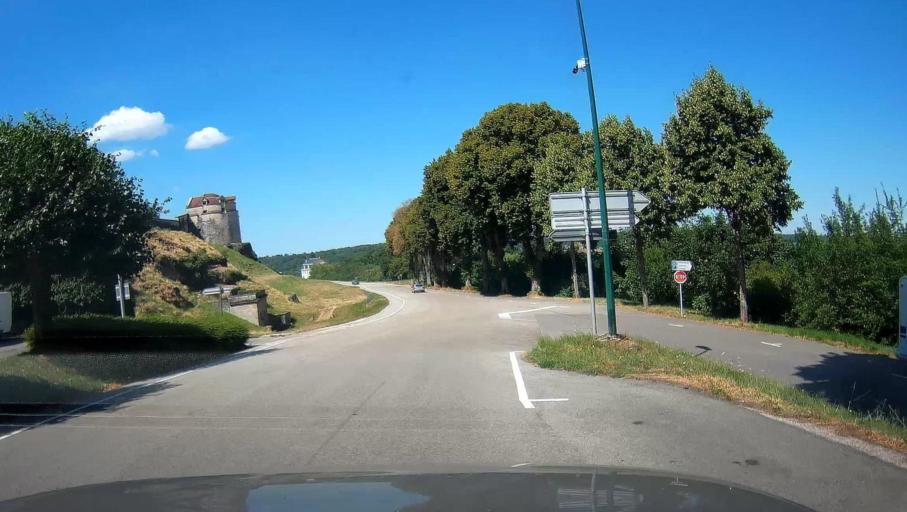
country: FR
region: Champagne-Ardenne
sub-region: Departement de la Haute-Marne
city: Langres
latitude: 47.8682
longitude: 5.3347
